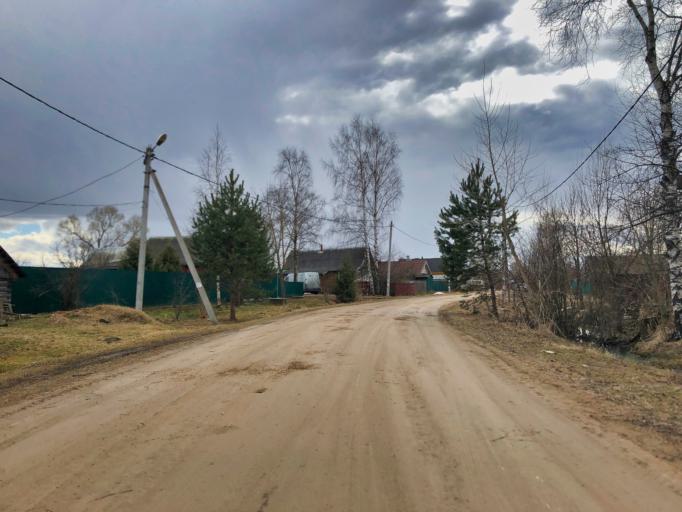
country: RU
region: Tverskaya
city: Rzhev
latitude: 56.2272
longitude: 34.3090
